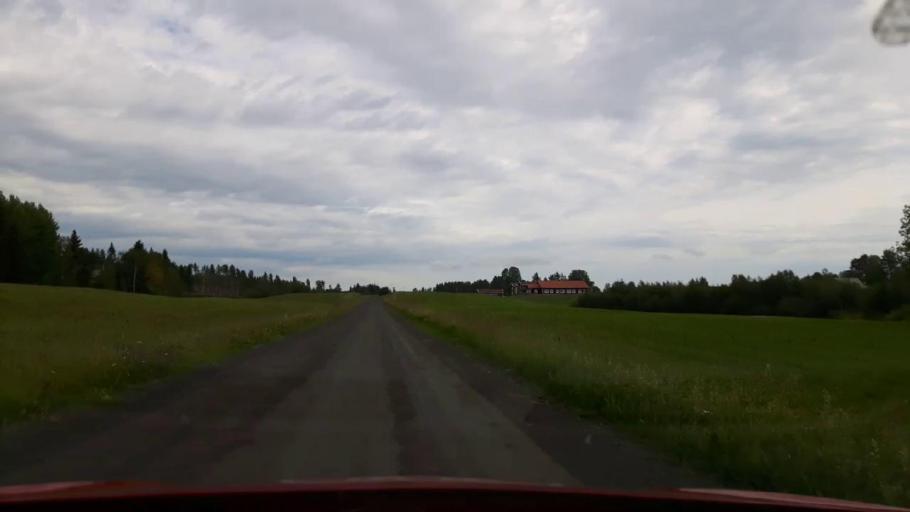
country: SE
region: Jaemtland
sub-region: OEstersunds Kommun
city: Lit
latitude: 63.4126
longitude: 15.2443
